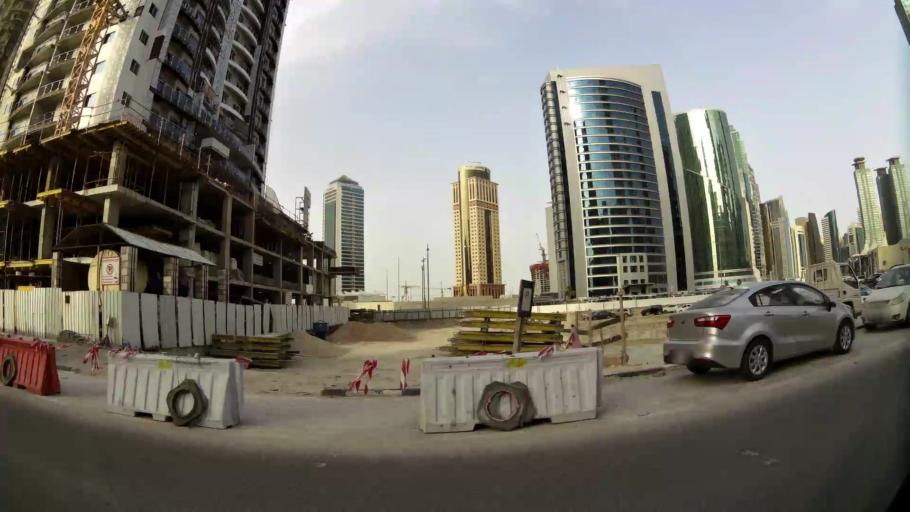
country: QA
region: Baladiyat ad Dawhah
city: Doha
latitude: 25.3267
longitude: 51.5256
